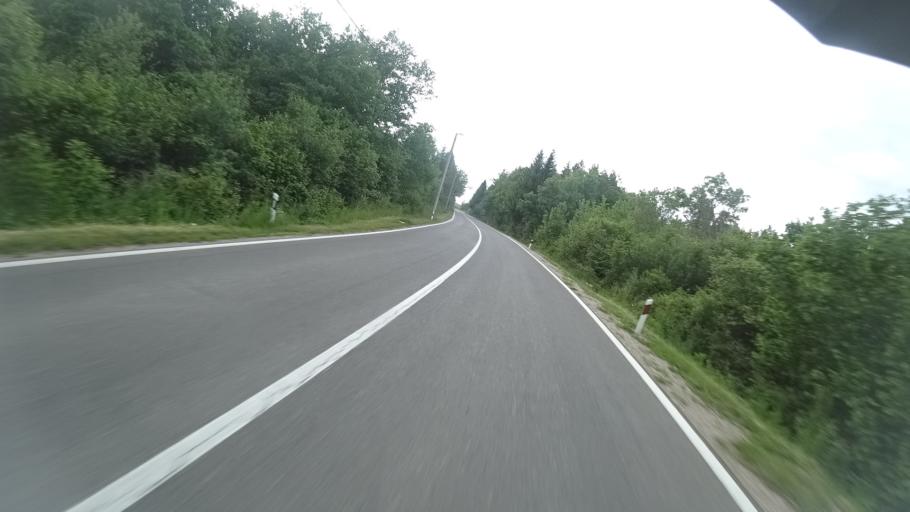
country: HR
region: Licko-Senjska
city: Gospic
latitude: 44.4949
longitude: 15.4598
